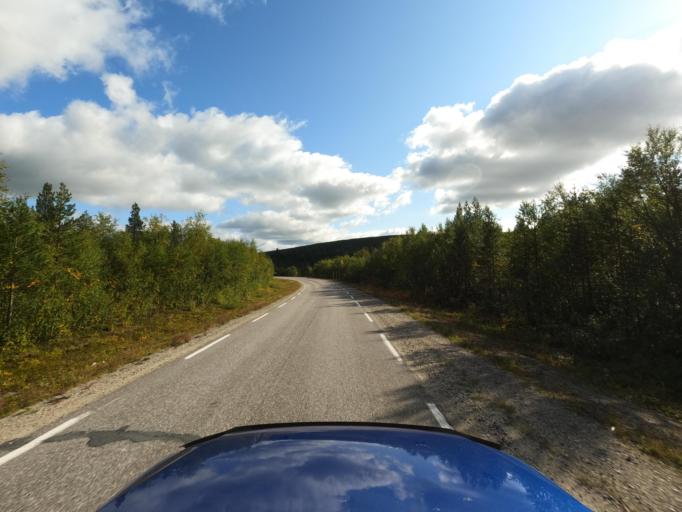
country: NO
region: Finnmark Fylke
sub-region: Karasjok
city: Karasjohka
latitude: 69.4272
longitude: 24.9392
